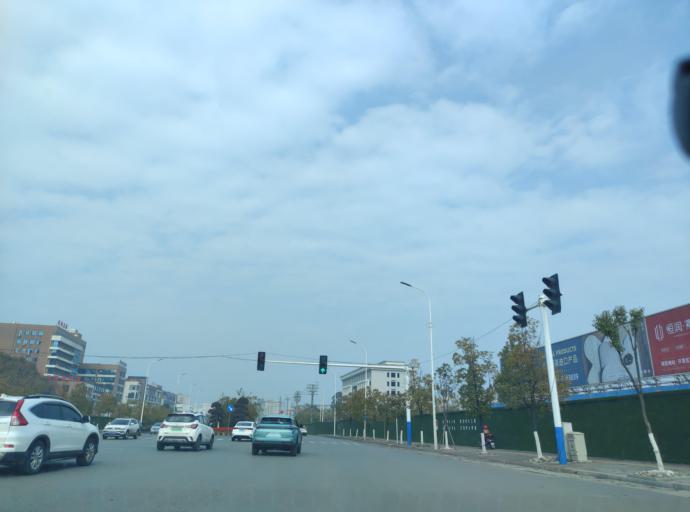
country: CN
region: Jiangxi Sheng
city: Pingxiang
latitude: 27.6375
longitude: 113.8813
